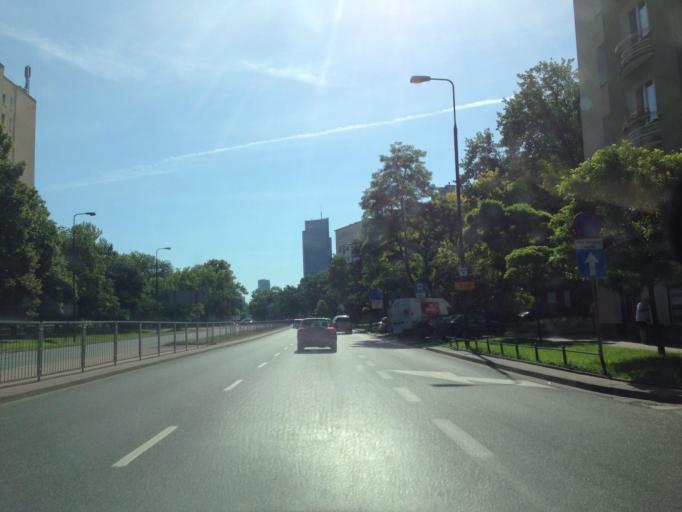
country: PL
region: Masovian Voivodeship
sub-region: Warszawa
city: Wola
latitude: 52.2370
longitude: 20.9664
